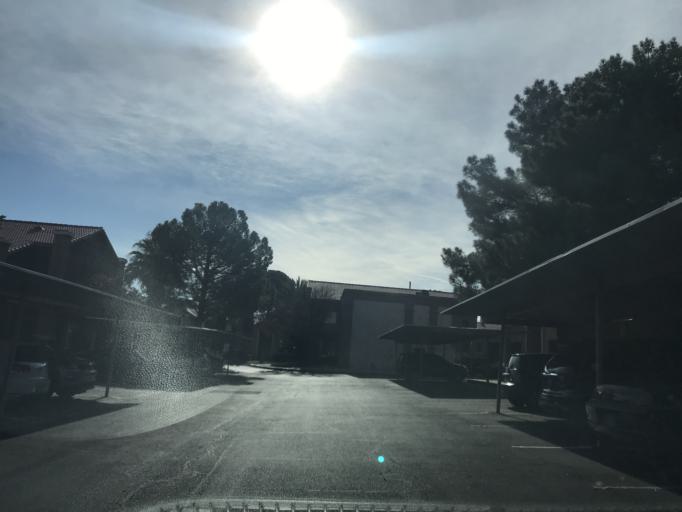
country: US
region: Nevada
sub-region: Clark County
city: Spring Valley
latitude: 36.0981
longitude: -115.2176
